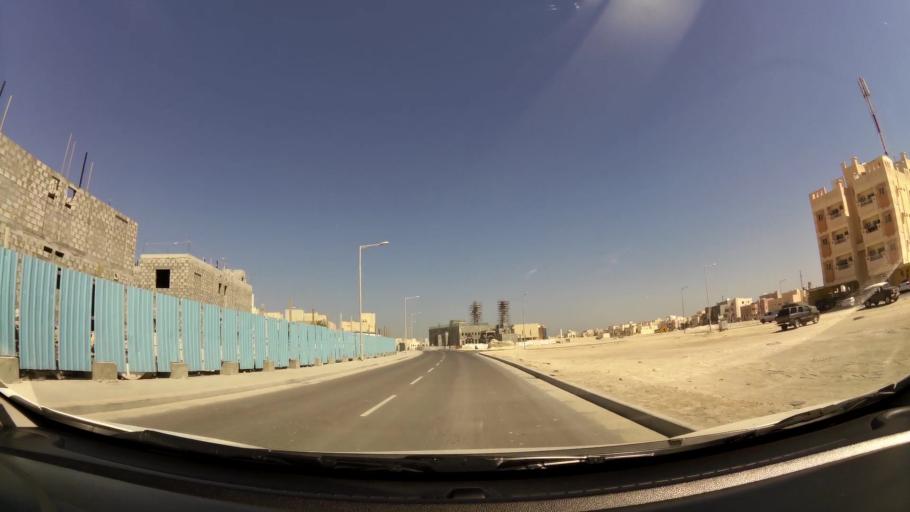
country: BH
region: Muharraq
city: Al Muharraq
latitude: 26.2738
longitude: 50.5986
